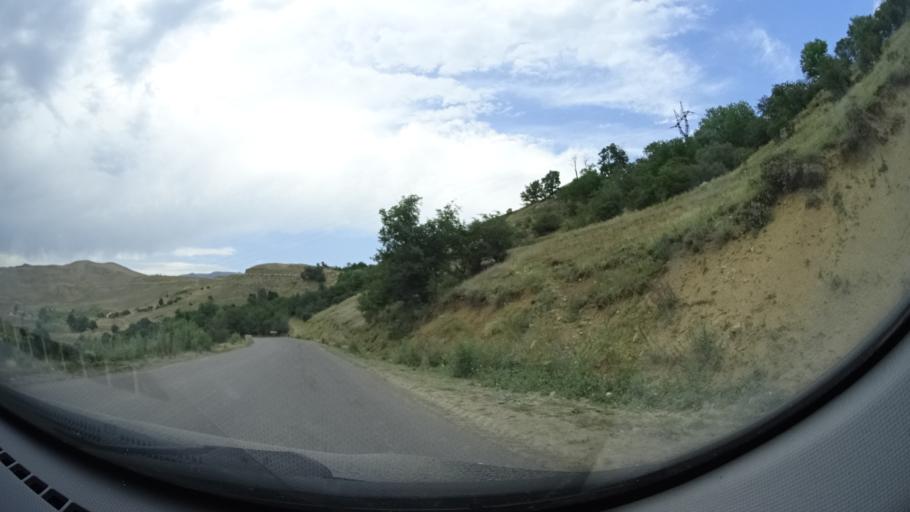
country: GE
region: Samtskhe-Javakheti
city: Aspindza
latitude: 41.5921
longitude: 43.2275
